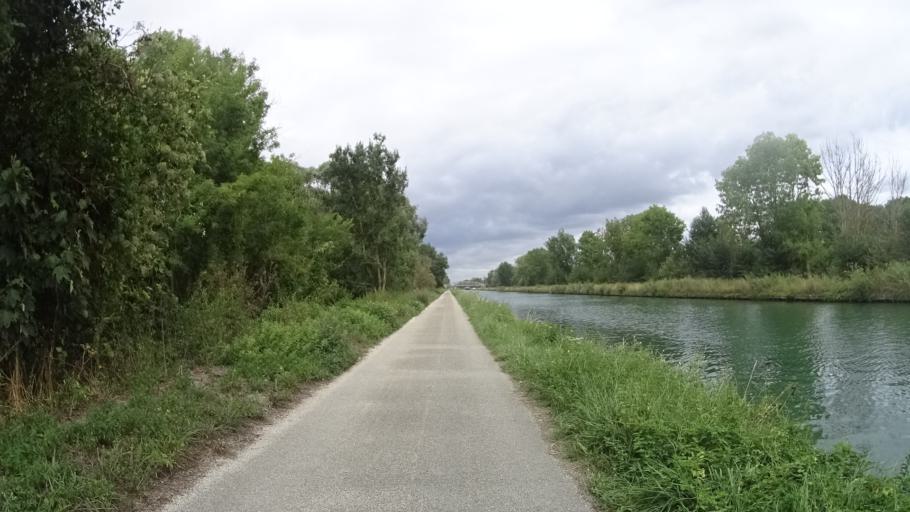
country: FR
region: Picardie
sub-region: Departement de l'Aisne
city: Viry-Noureuil
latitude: 49.6203
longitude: 3.2479
